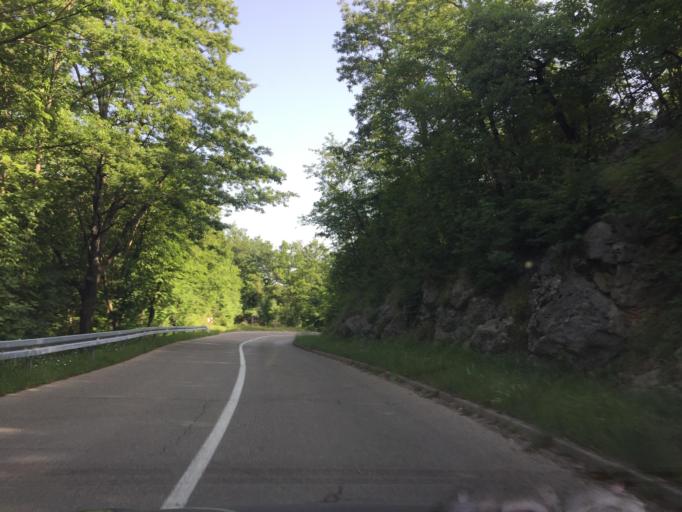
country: HR
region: Primorsko-Goranska
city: Klana
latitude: 45.4303
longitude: 14.3674
